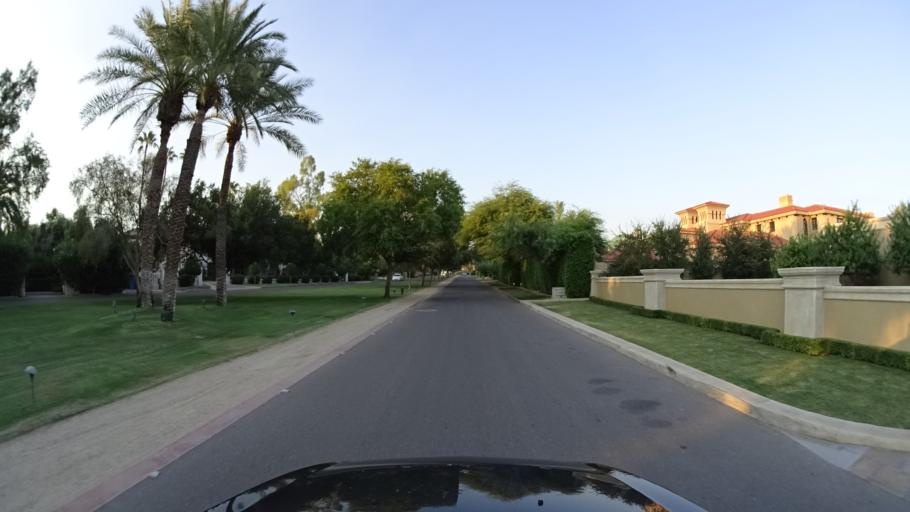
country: US
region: Arizona
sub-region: Maricopa County
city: Paradise Valley
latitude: 33.5188
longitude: -112.0253
